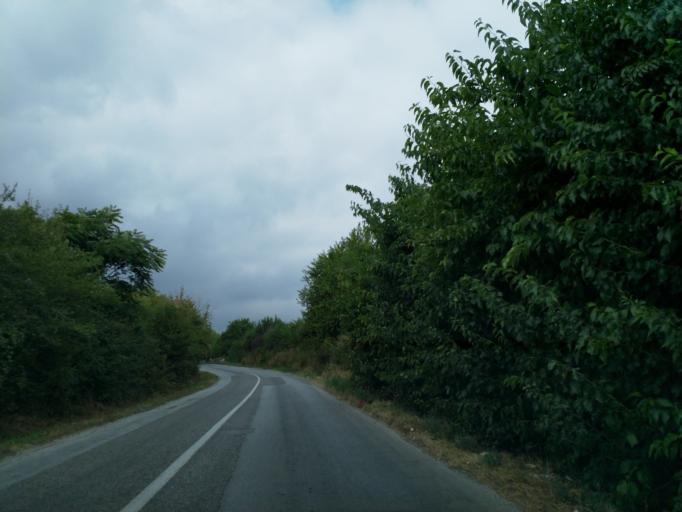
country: RS
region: Central Serbia
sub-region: Pomoravski Okrug
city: Jagodina
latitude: 43.9885
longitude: 21.2355
